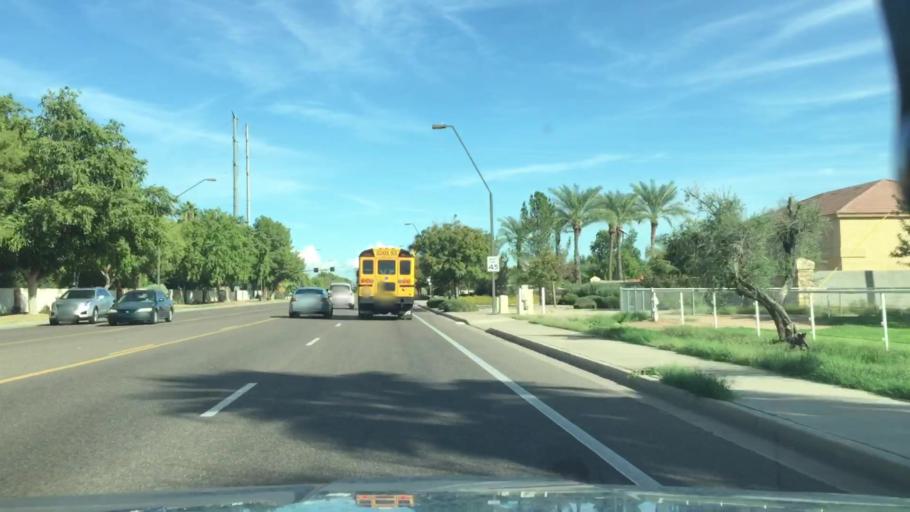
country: US
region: Arizona
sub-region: Maricopa County
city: Gilbert
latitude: 33.3501
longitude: -111.7495
